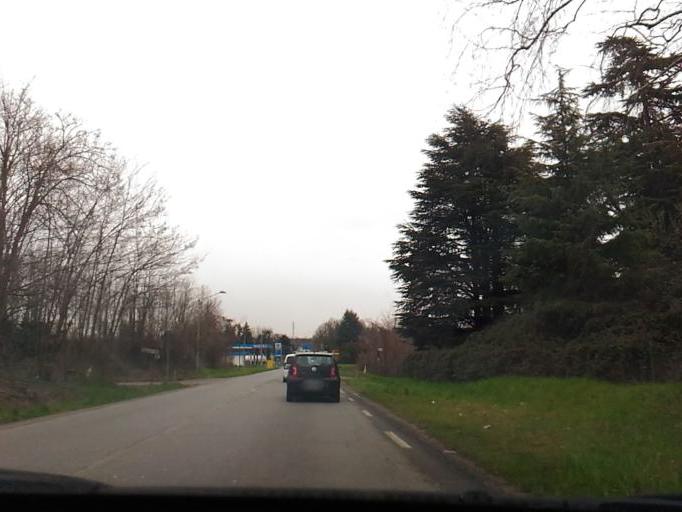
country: IT
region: Lombardy
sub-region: Provincia di Como
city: Mariano Comense
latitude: 45.7049
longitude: 9.1640
